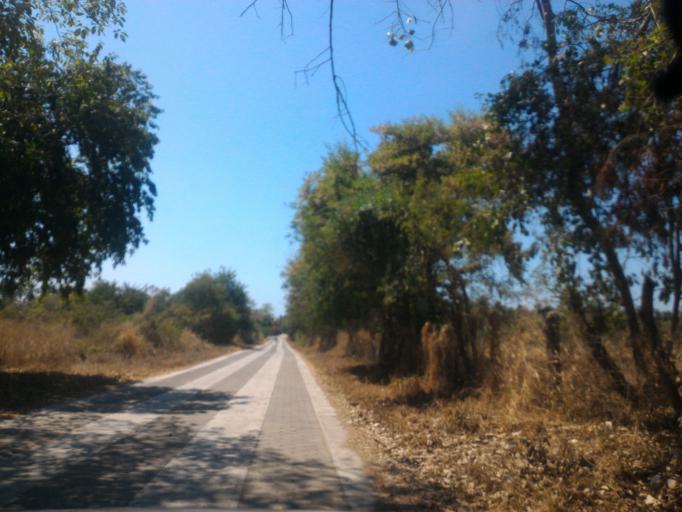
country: MX
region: Michoacan
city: Coahuayana Viejo
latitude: 18.5856
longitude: -103.6727
